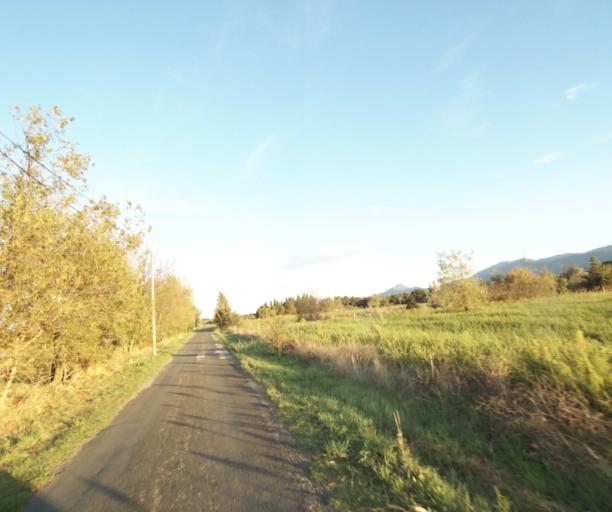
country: FR
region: Languedoc-Roussillon
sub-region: Departement des Pyrenees-Orientales
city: Latour-Bas-Elne
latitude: 42.5840
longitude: 2.9917
